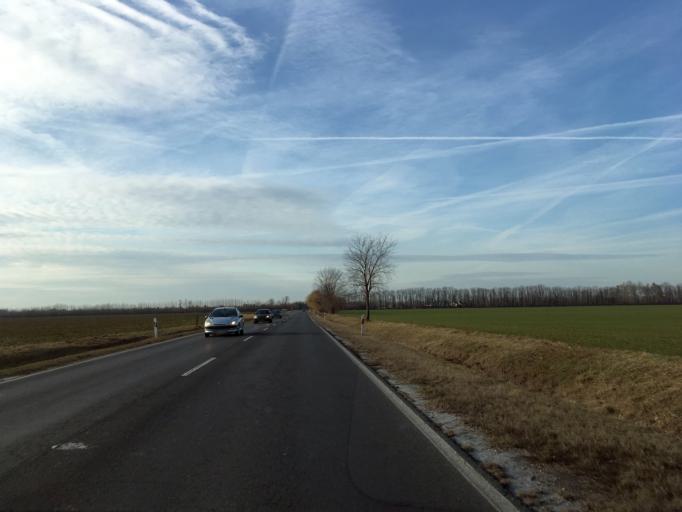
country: HU
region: Gyor-Moson-Sopron
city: Otteveny
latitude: 47.7134
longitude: 17.5146
